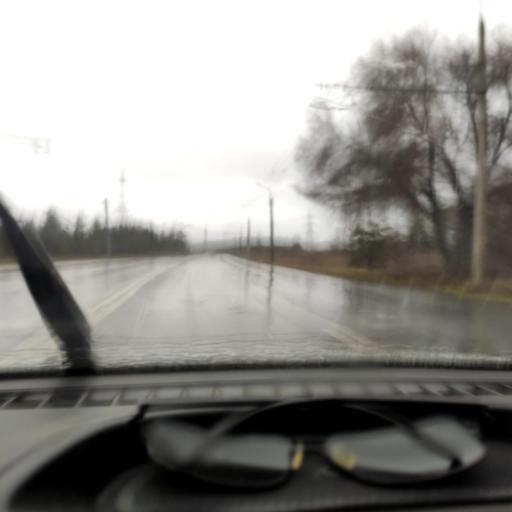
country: RU
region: Samara
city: Zhigulevsk
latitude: 53.4993
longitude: 49.5118
